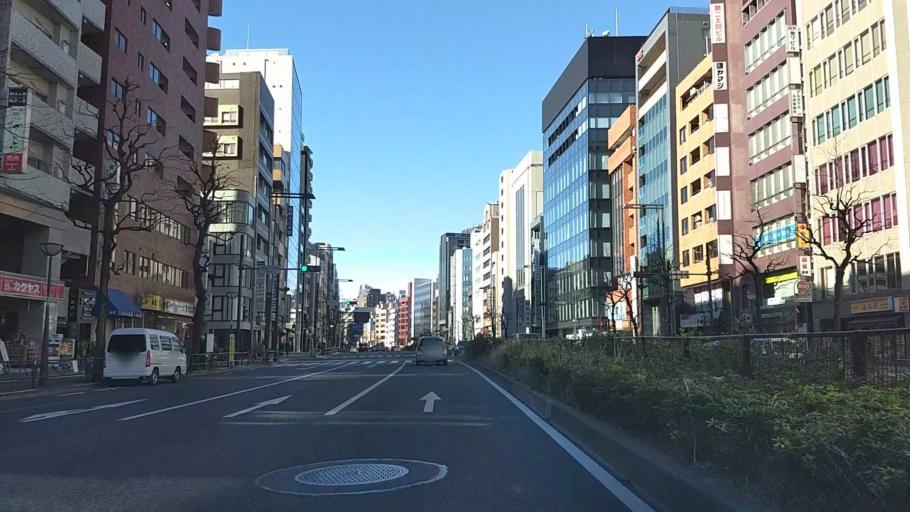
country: JP
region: Tokyo
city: Tokyo
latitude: 35.6872
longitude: 139.7257
